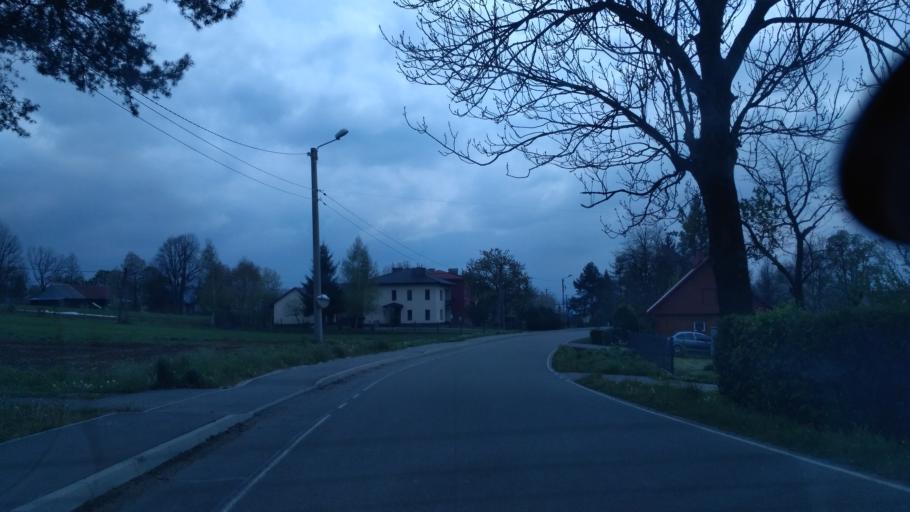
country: PL
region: Subcarpathian Voivodeship
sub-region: Powiat brzozowski
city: Haczow
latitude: 49.6575
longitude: 21.9088
